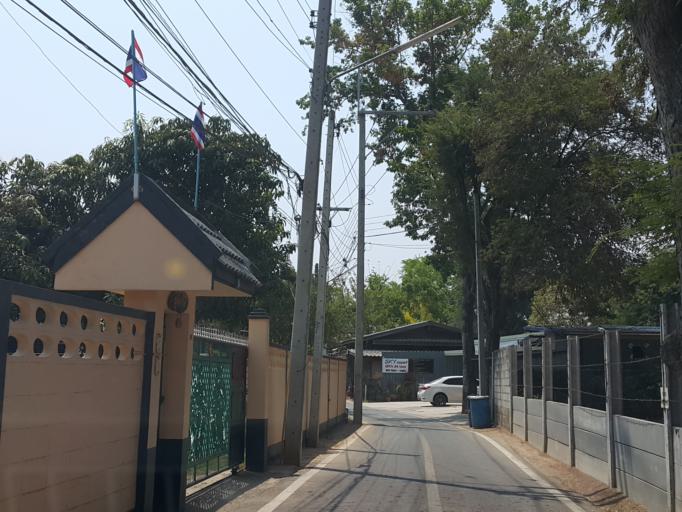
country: TH
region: Kanchanaburi
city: Kanchanaburi
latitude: 14.0307
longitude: 99.5217
